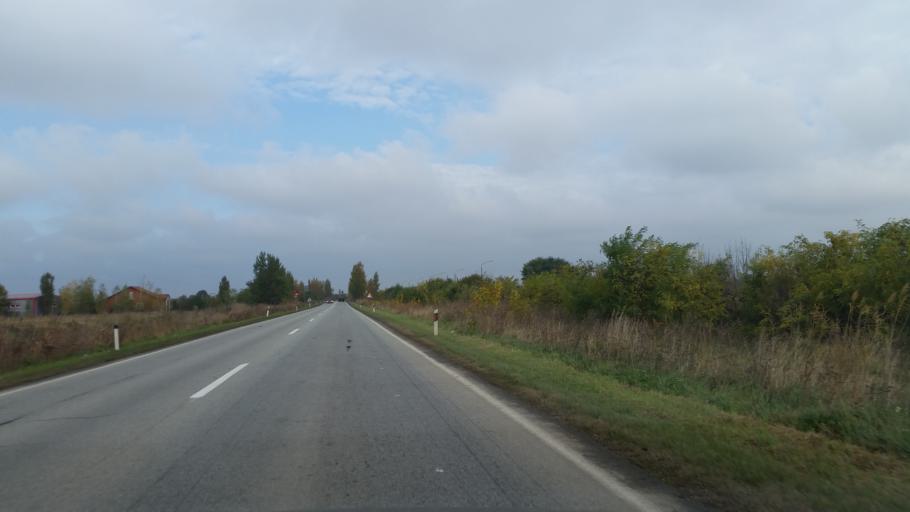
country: RS
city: Melenci
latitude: 45.5006
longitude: 20.3245
